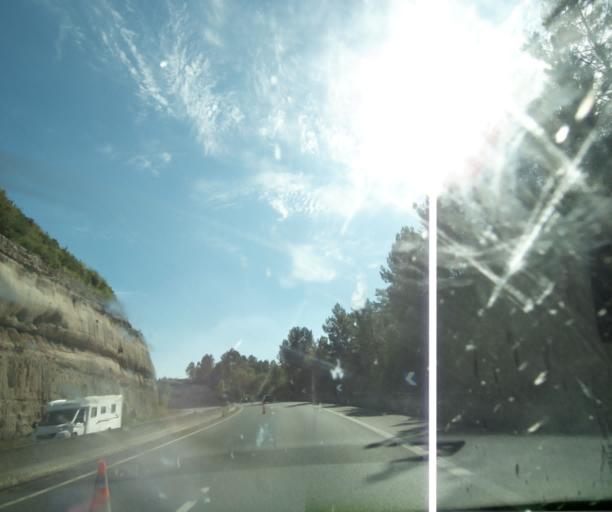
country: FR
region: Limousin
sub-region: Departement de la Correze
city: Brive-la-Gaillarde
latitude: 45.1140
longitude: 1.4997
